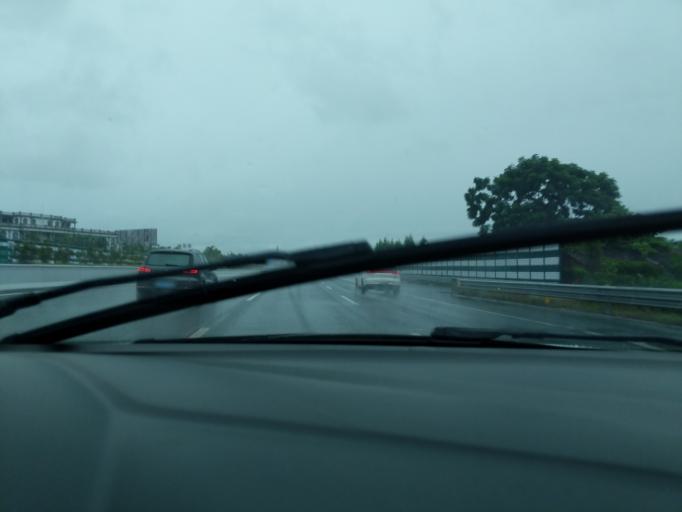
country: CN
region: Guangdong
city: Shuikou
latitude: 22.4821
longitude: 112.7749
